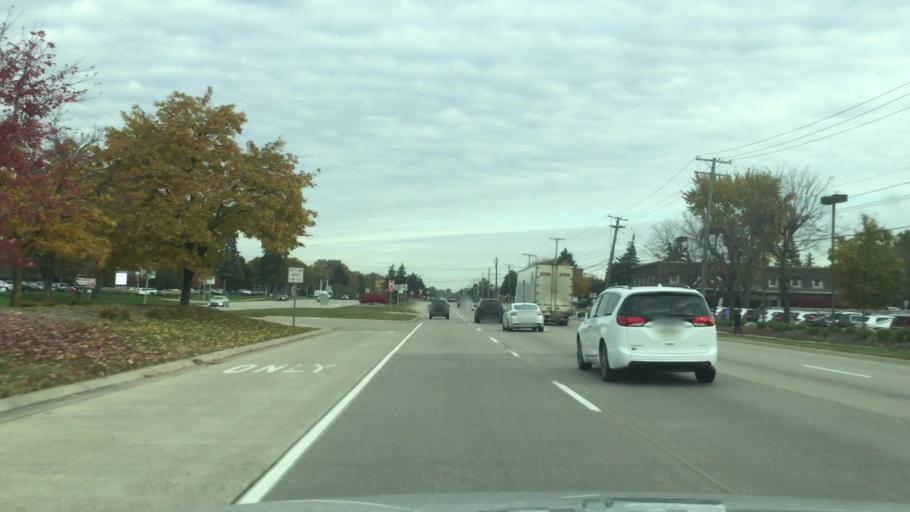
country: US
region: Michigan
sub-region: Oakland County
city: Bingham Farms
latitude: 42.5043
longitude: -83.2852
